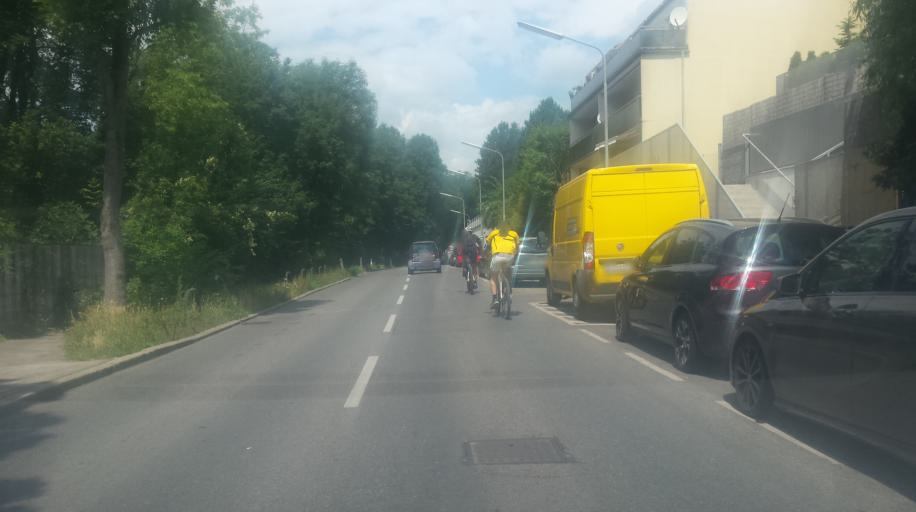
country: AT
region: Lower Austria
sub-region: Politischer Bezirk Wien-Umgebung
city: Purkersdorf
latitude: 48.2152
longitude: 16.2210
